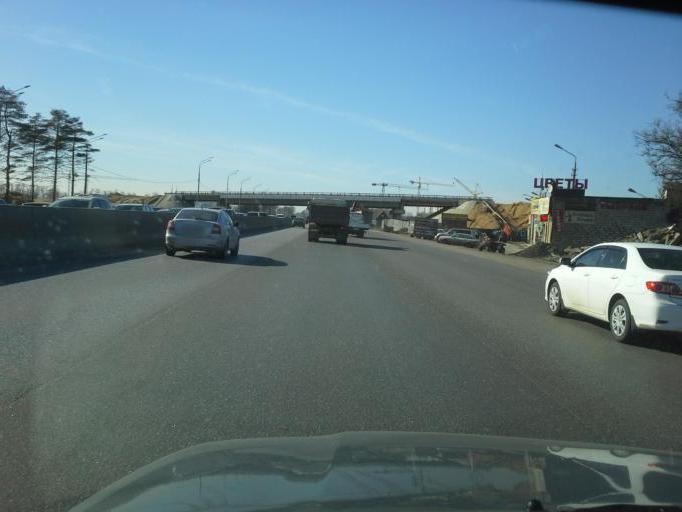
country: RU
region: Moskovskaya
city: Novoivanovskoye
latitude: 55.7027
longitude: 37.3514
